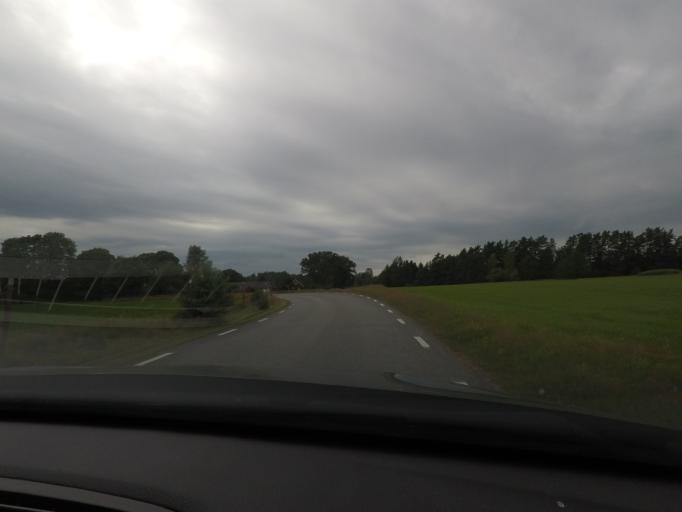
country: SE
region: Kronoberg
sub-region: Markaryds Kommun
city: Stromsnasbruk
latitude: 56.4240
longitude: 13.7742
